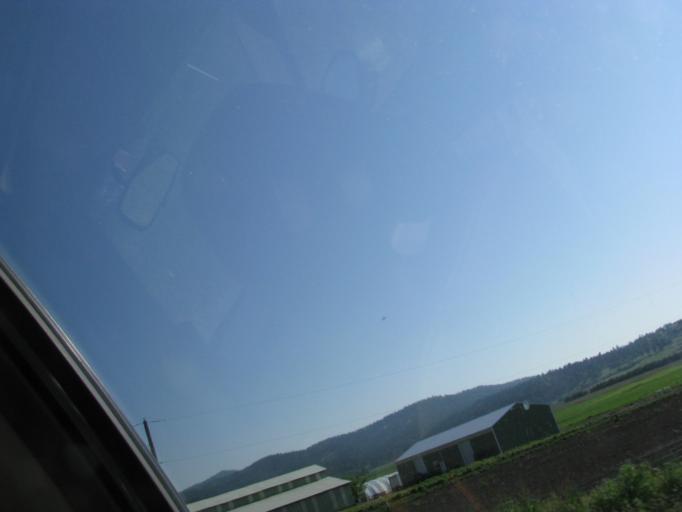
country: US
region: Washington
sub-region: Spokane County
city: Liberty Lake
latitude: 47.6278
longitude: -117.1140
